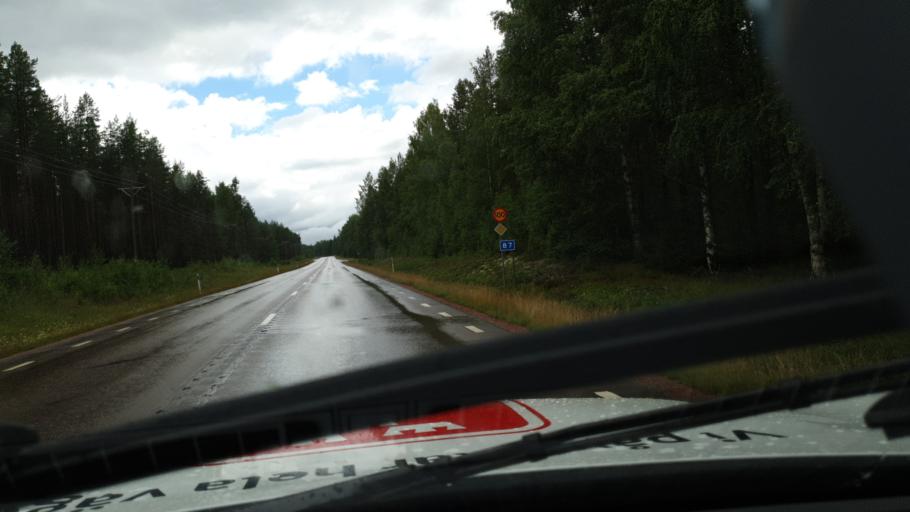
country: SE
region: Jaemtland
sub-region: Ragunda Kommun
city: Hammarstrand
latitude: 63.1730
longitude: 15.8743
